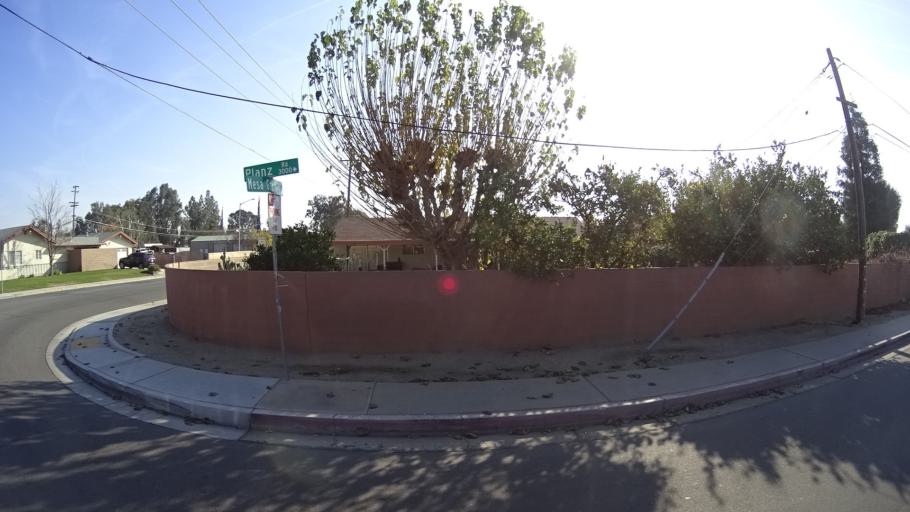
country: US
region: California
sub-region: Kern County
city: Bakersfield
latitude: 35.3249
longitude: -119.0347
